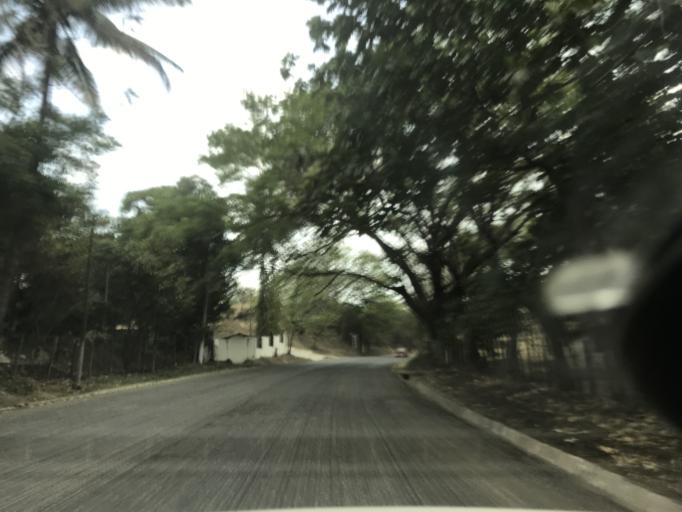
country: GT
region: Zacapa
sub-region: Municipio de Zacapa
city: Gualan
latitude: 15.1785
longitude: -89.3024
